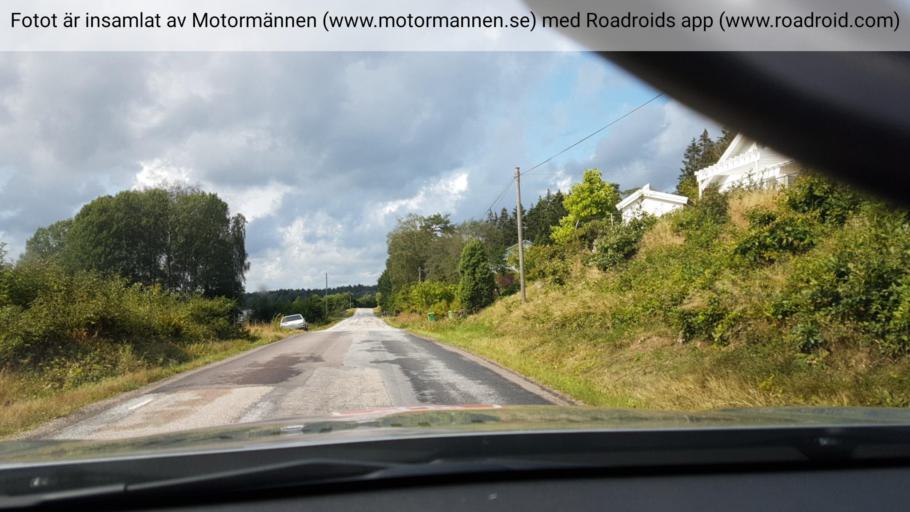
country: SE
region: Vaestra Goetaland
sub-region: Uddevalla Kommun
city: Ljungskile
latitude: 58.2411
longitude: 11.8681
